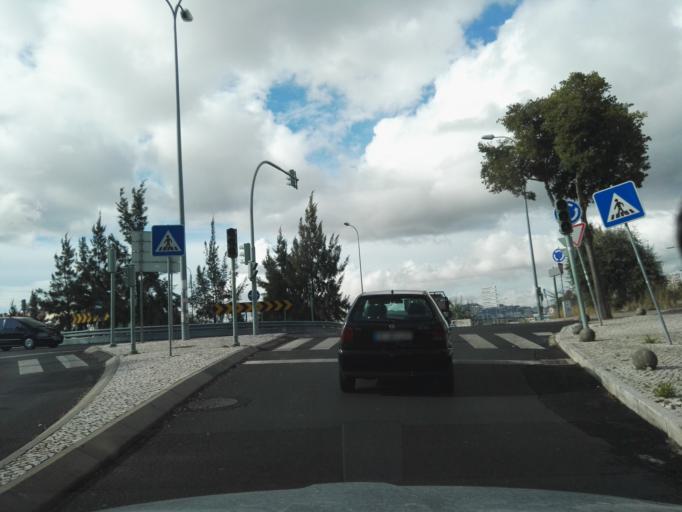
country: PT
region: Lisbon
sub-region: Odivelas
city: Pontinha
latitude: 38.7569
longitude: -9.2047
